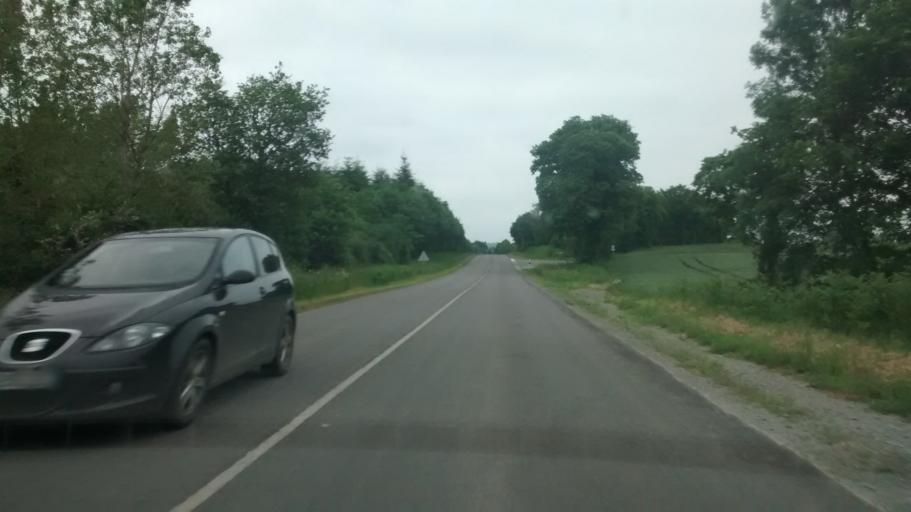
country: FR
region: Brittany
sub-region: Departement du Morbihan
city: Campeneac
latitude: 47.9511
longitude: -2.3064
